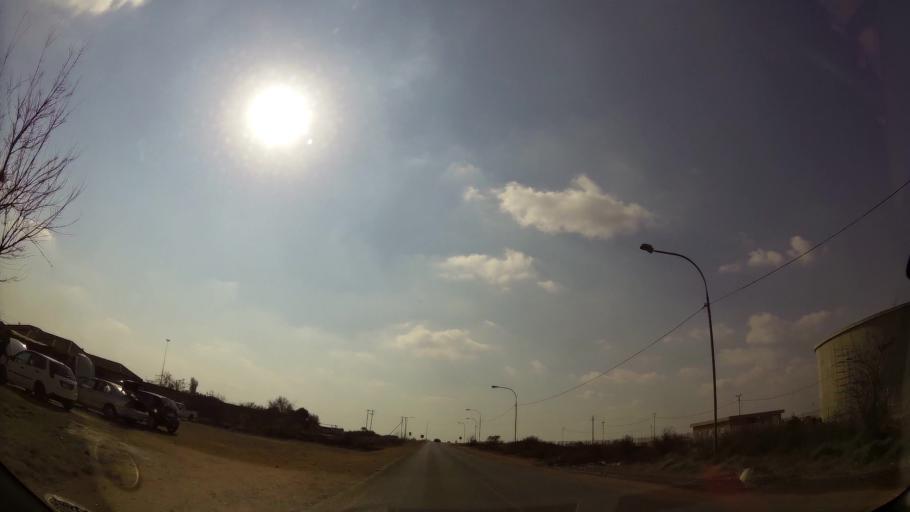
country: ZA
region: Gauteng
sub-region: Ekurhuleni Metropolitan Municipality
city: Springs
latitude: -26.1273
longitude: 28.4891
